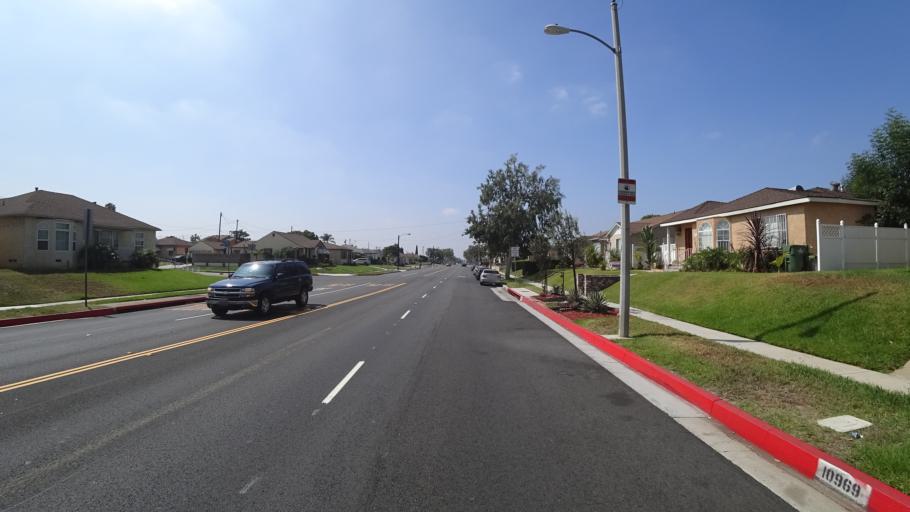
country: US
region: California
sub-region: Los Angeles County
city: Westmont
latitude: 33.9354
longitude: -118.3178
